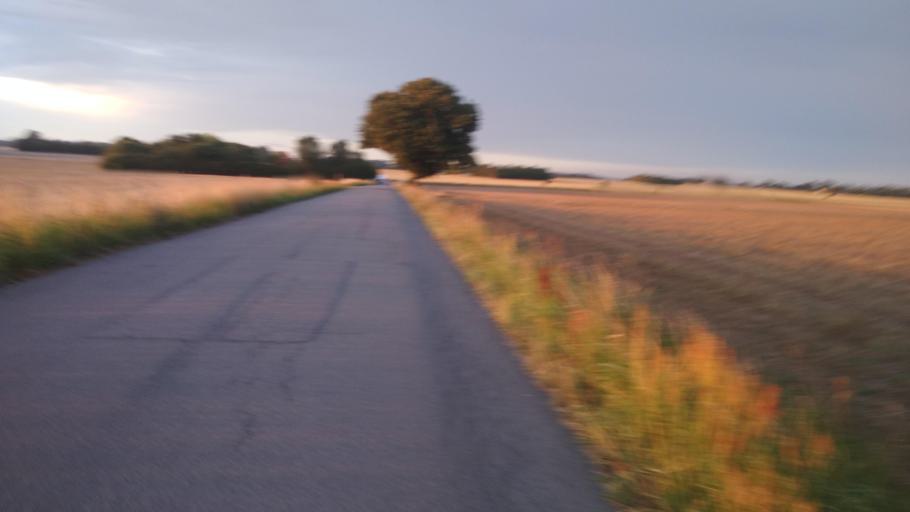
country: DK
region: Capital Region
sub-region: Bornholm Kommune
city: Akirkeby
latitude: 55.0320
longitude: 14.9140
